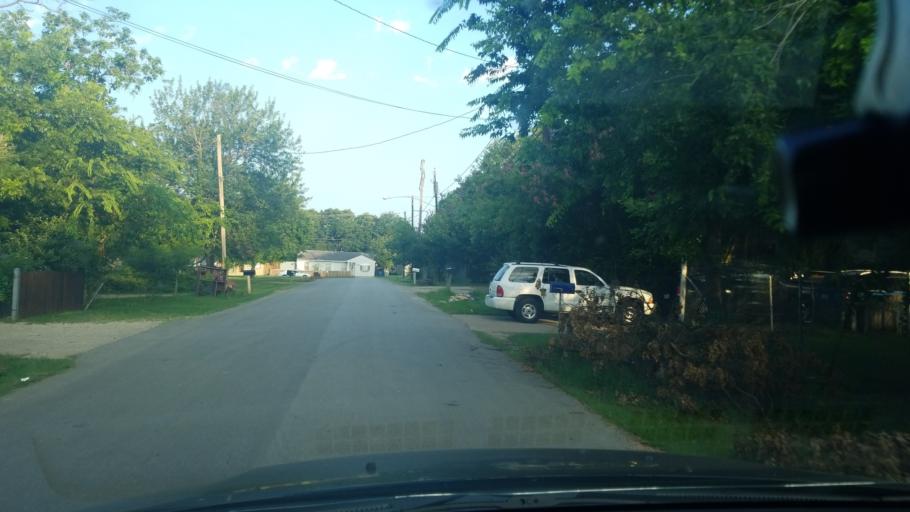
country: US
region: Texas
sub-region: Dallas County
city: Balch Springs
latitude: 32.7237
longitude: -96.6558
